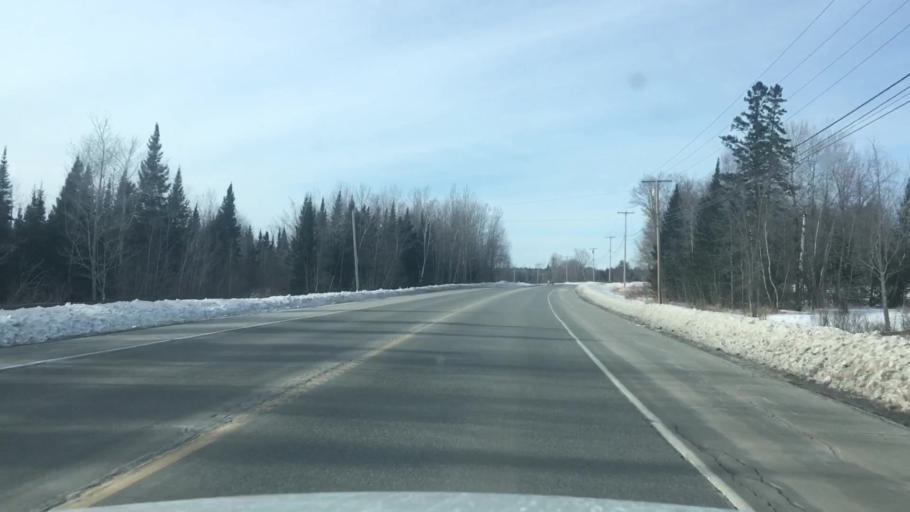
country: US
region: Maine
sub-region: Penobscot County
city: Kenduskeag
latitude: 44.9077
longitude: -68.8944
